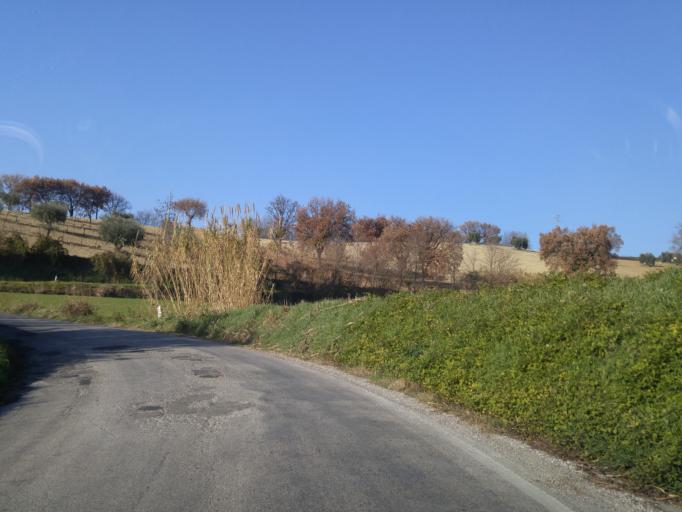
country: IT
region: The Marches
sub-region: Provincia di Pesaro e Urbino
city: Montefelcino
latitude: 43.7243
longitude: 12.8406
